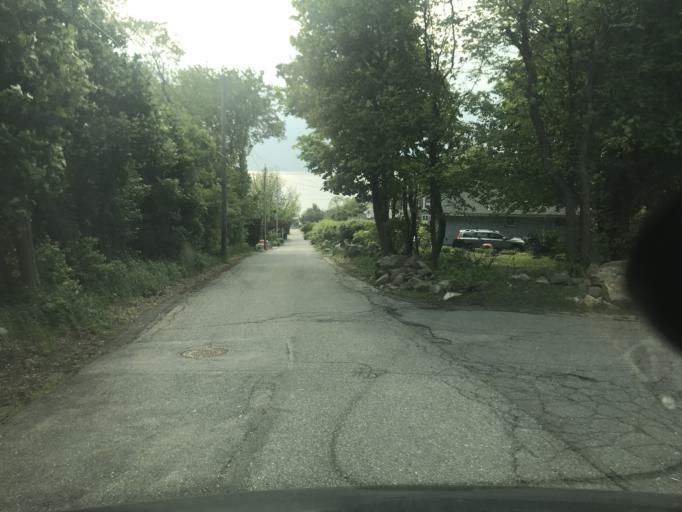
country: US
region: Massachusetts
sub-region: Essex County
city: Rockport
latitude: 42.6721
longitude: -70.6272
